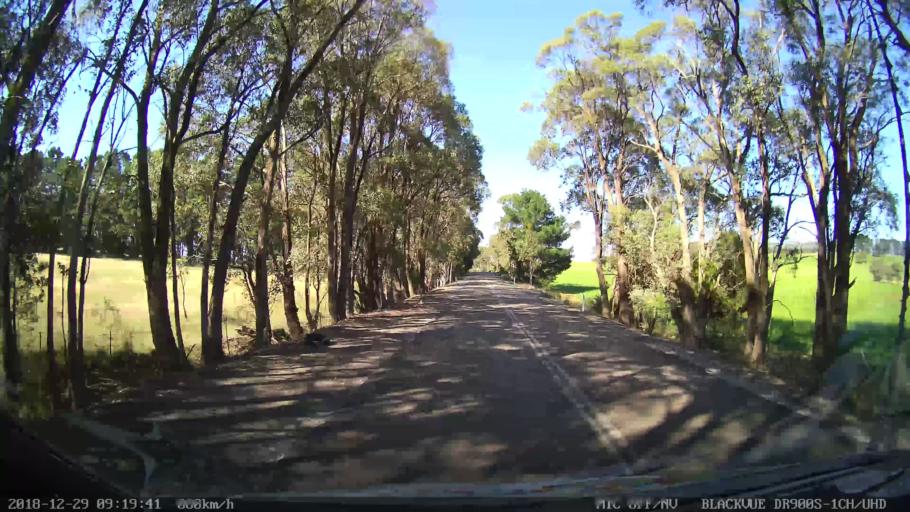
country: AU
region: New South Wales
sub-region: Upper Lachlan Shire
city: Crookwell
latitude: -34.4841
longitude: 149.4274
